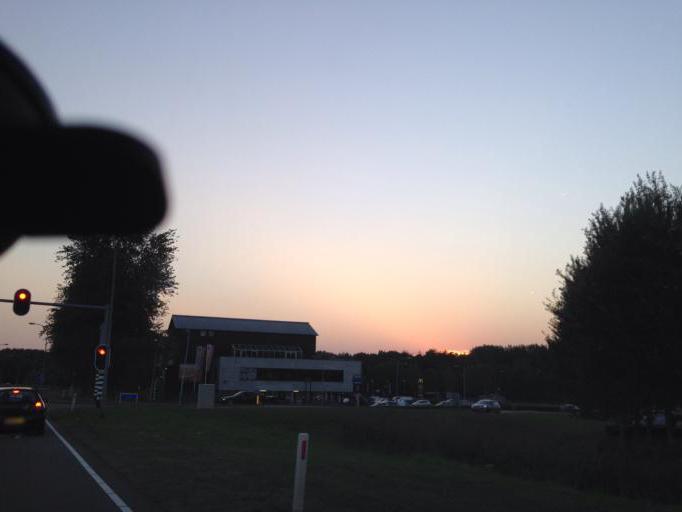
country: NL
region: Flevoland
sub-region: Gemeente Almere
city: Almere Stad
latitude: 52.3557
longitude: 5.2142
